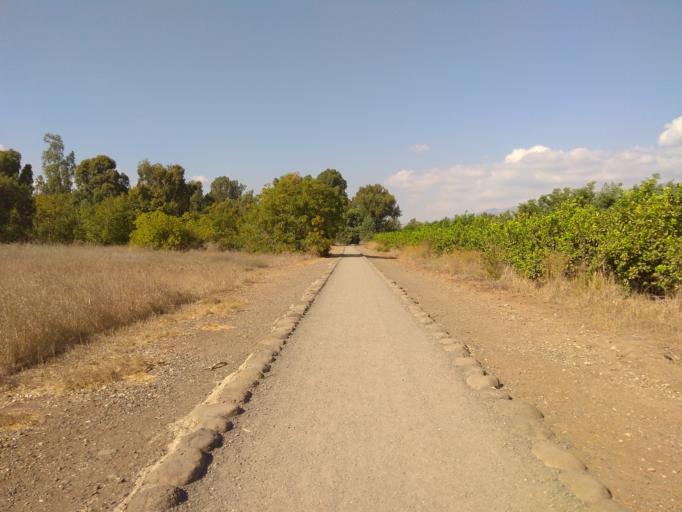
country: IL
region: Northern District
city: Qiryat Shemona
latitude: 33.2246
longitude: 35.6158
